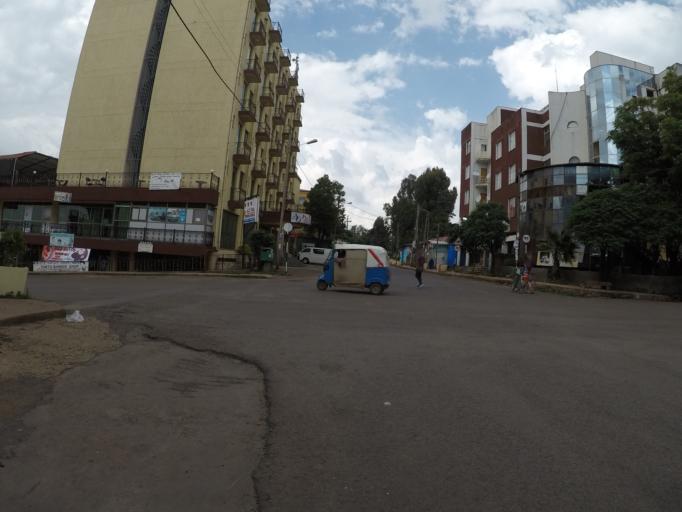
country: ET
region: Amhara
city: Gondar
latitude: 12.6153
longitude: 37.4723
